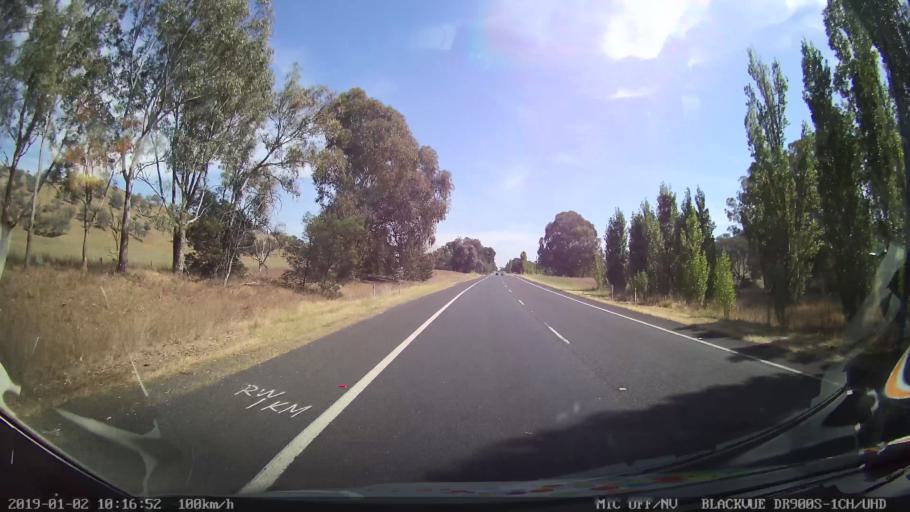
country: AU
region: New South Wales
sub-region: Gundagai
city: Gundagai
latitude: -35.0332
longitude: 148.1089
